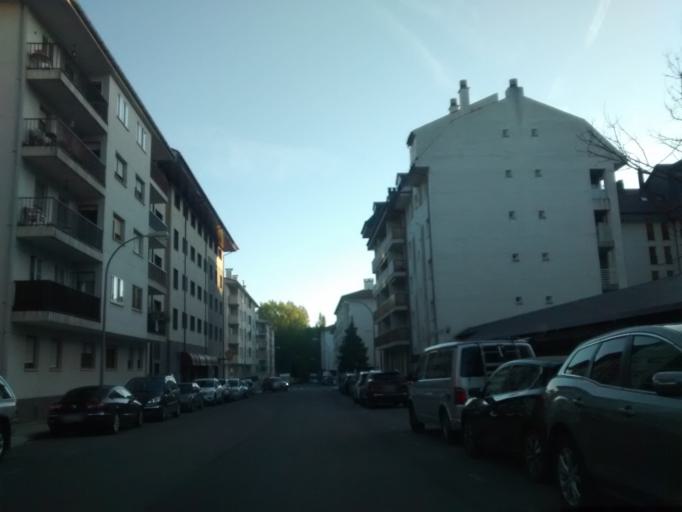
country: ES
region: Aragon
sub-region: Provincia de Huesca
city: Jaca
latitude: 42.5700
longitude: -0.5443
